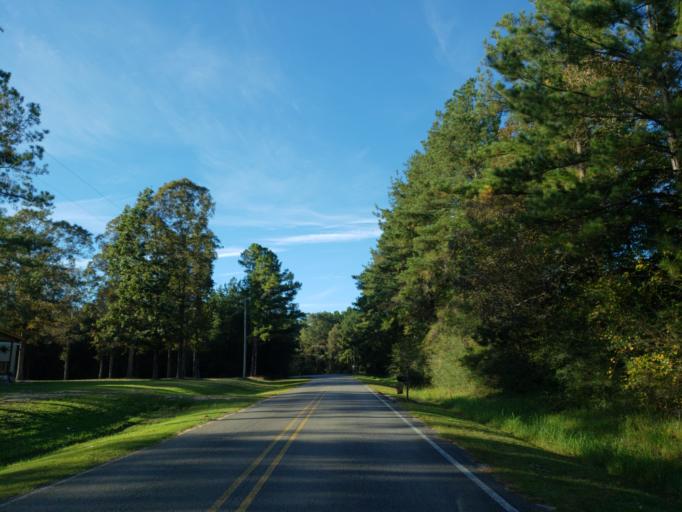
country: US
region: Mississippi
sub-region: Perry County
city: Richton
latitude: 31.3476
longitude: -88.8114
